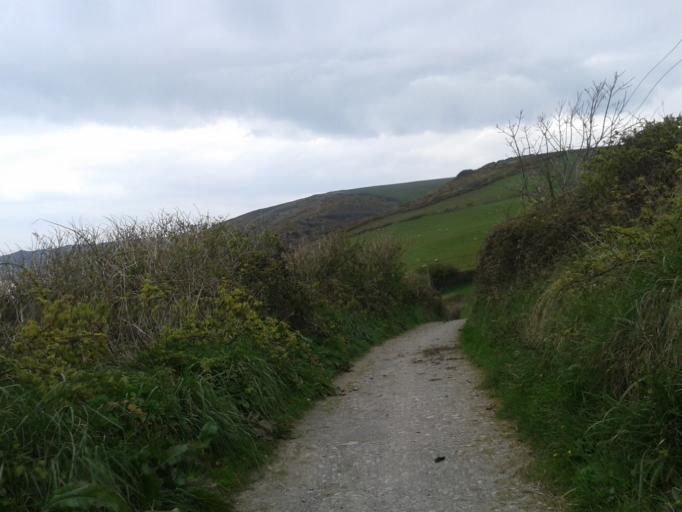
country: GB
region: England
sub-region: Devon
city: Braunton
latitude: 51.1463
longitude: -4.2169
